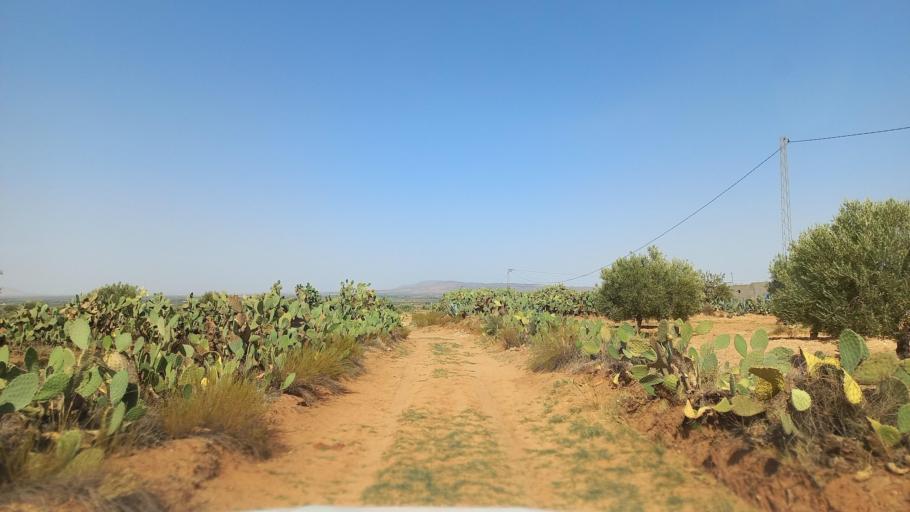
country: TN
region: Al Qasrayn
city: Kasserine
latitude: 35.2051
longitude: 9.0200
